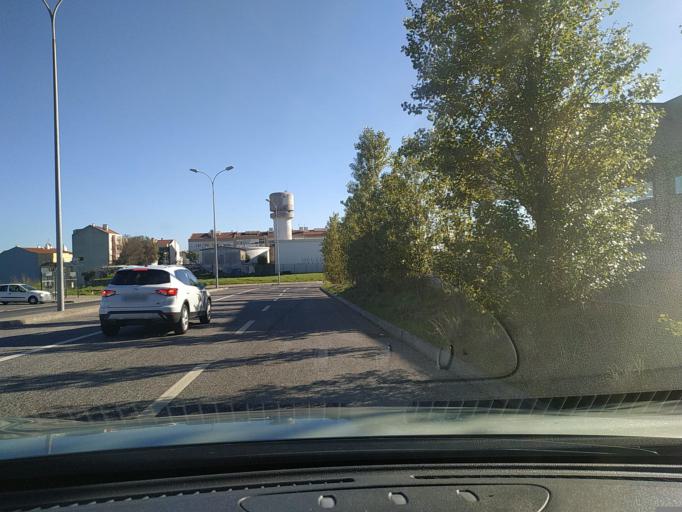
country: PT
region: Lisbon
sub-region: Amadora
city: Amadora
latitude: 38.7702
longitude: -9.2246
